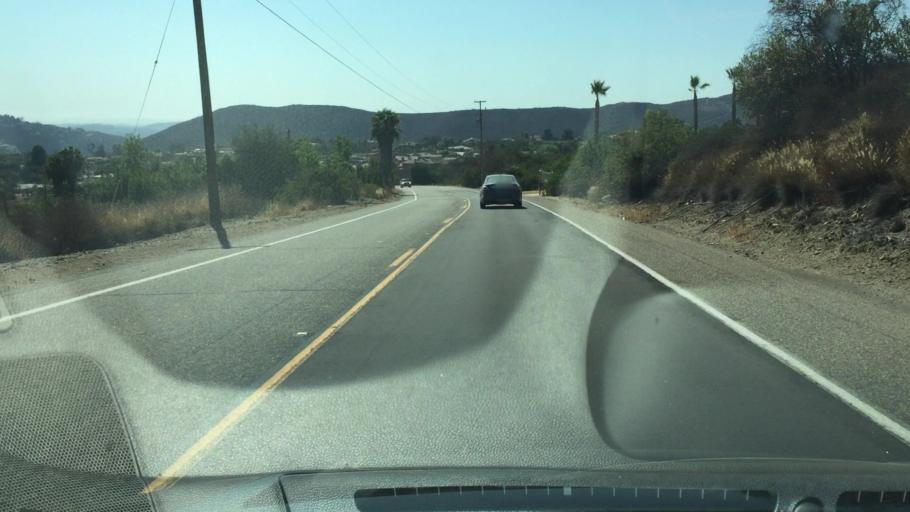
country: US
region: California
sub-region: San Diego County
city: Jamul
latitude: 32.7354
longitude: -116.8427
